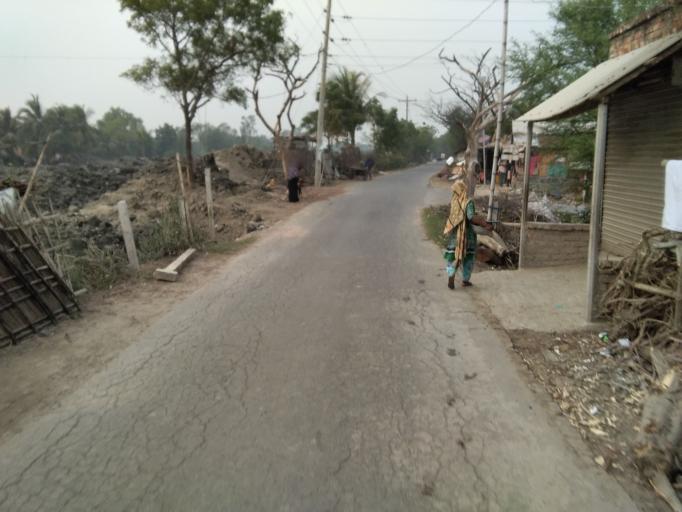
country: BD
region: Khulna
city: Satkhira
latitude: 22.5831
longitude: 89.0670
